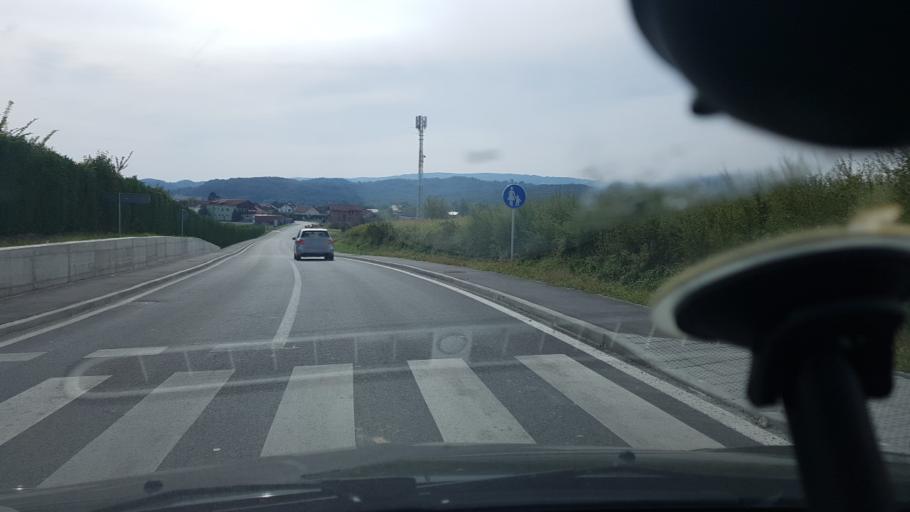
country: HR
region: Krapinsko-Zagorska
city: Marija Bistrica
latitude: 46.0564
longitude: 16.1647
